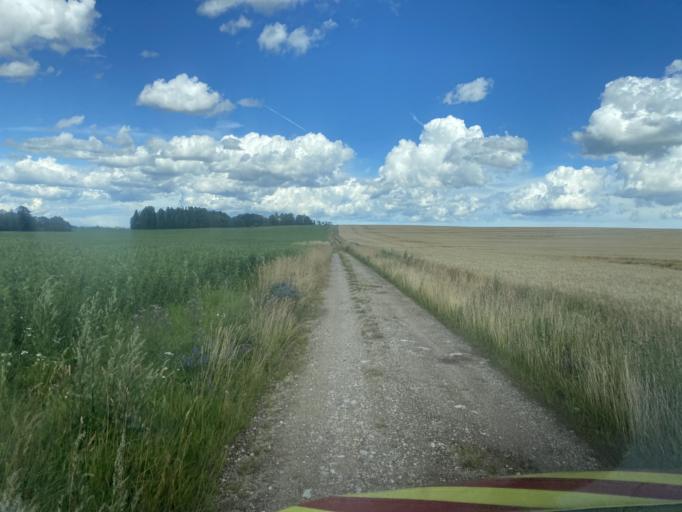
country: EE
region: Viljandimaa
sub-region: Viljandi linn
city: Viljandi
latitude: 58.2898
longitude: 25.5996
